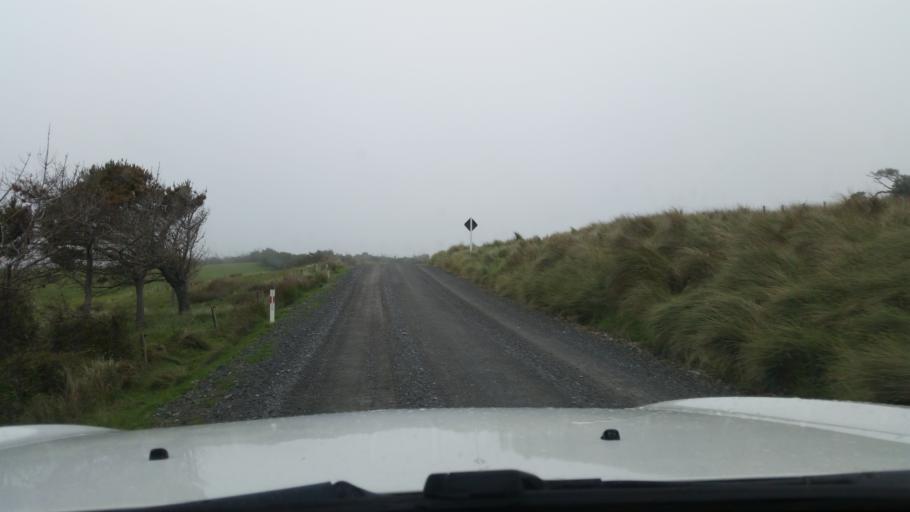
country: NZ
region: Chatham Islands
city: Waitangi
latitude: -43.8084
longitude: -176.6015
